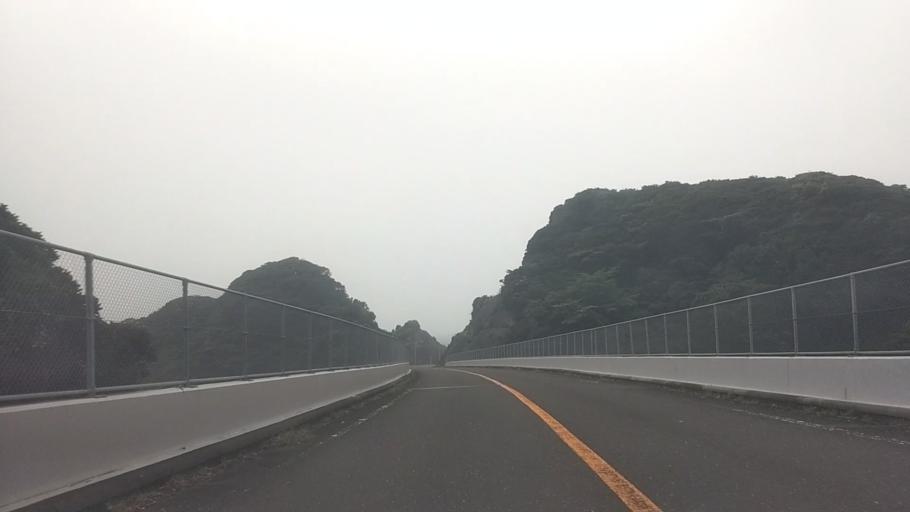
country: JP
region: Chiba
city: Katsuura
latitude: 35.1548
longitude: 140.3060
